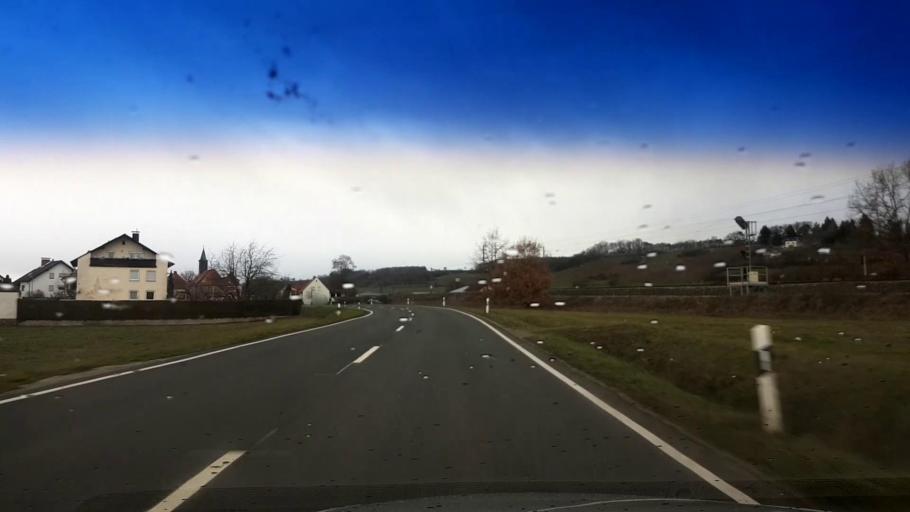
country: DE
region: Bavaria
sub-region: Upper Franconia
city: Oberhaid
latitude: 49.9336
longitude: 10.7957
